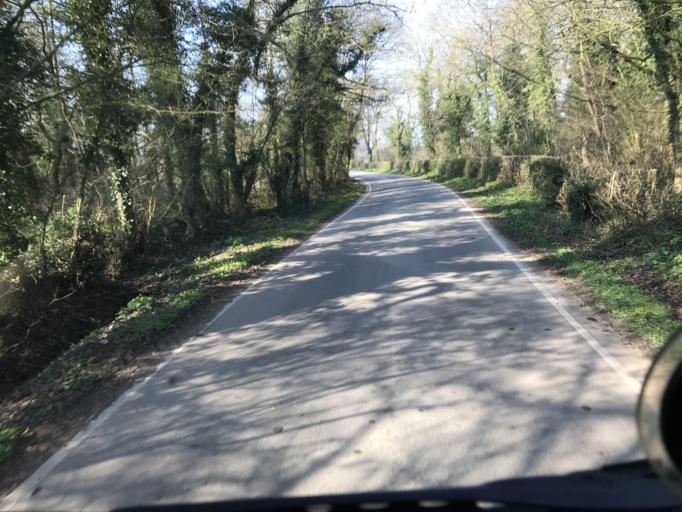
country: GB
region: England
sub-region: Cheshire West and Chester
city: Waverton
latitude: 53.1395
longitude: -2.8257
